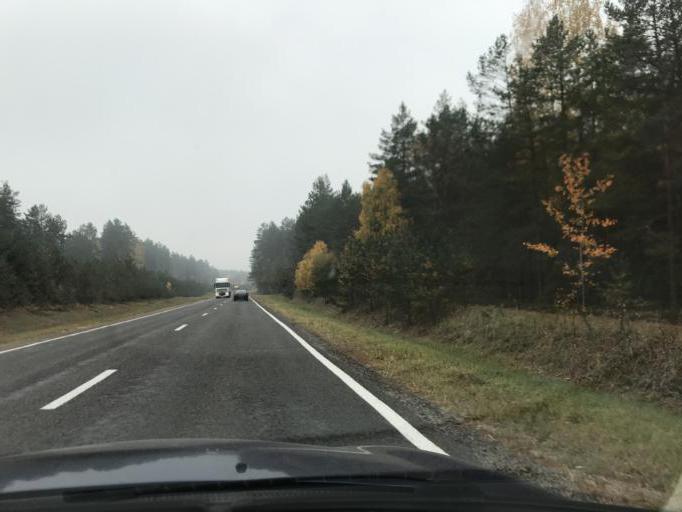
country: LT
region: Alytaus apskritis
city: Druskininkai
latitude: 53.8918
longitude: 23.9113
